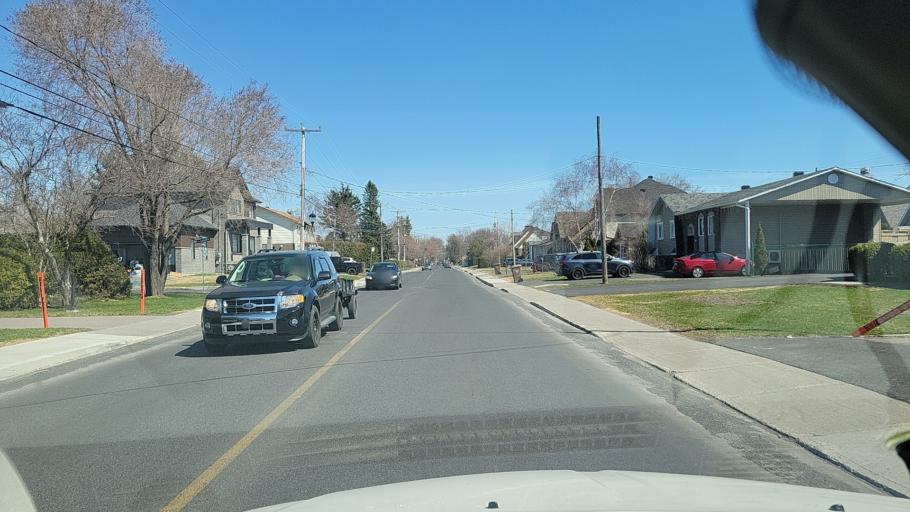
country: CA
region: Quebec
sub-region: Monteregie
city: Sainte-Julie
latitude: 45.5894
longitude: -73.3451
